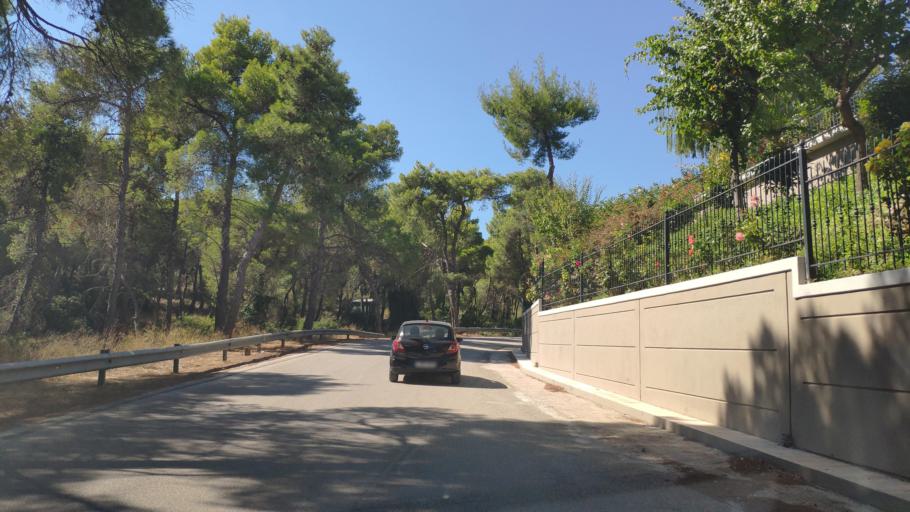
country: GR
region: Attica
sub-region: Nomarchia Anatolikis Attikis
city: Kouvaras
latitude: 37.8408
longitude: 24.0013
